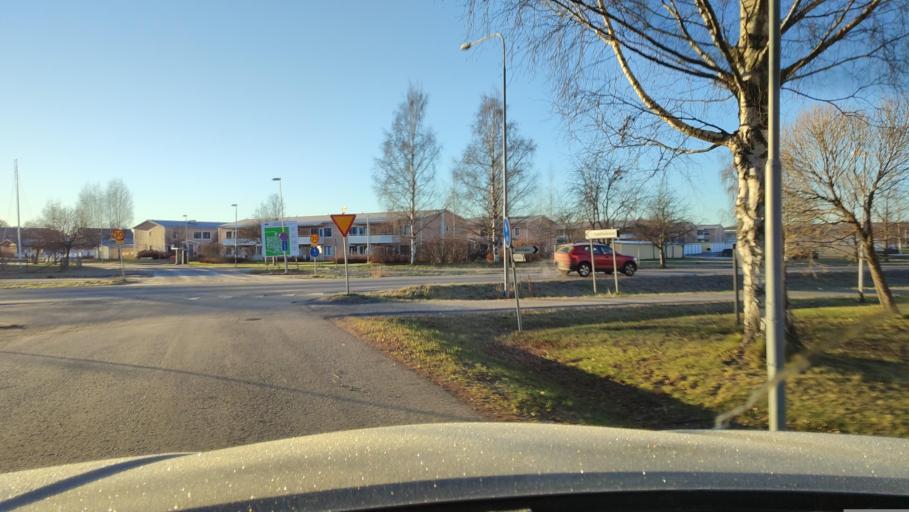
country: SE
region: Vaesterbotten
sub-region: Skelleftea Kommun
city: Skelleftea
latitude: 64.7452
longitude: 20.9829
